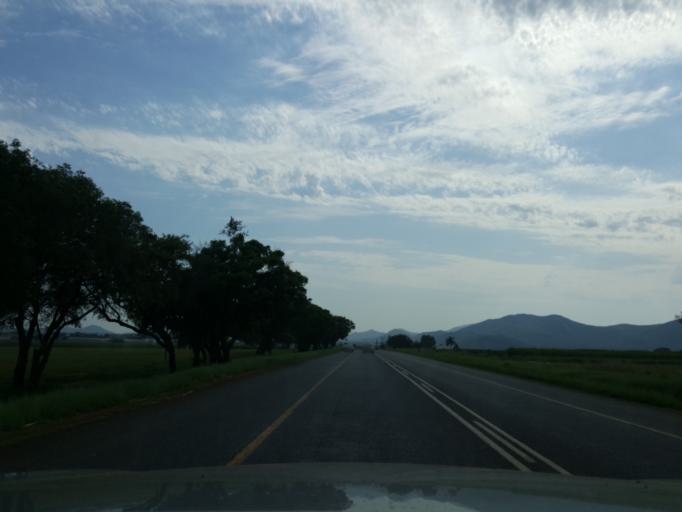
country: SZ
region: Hhohho
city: Ntfonjeni
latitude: -25.5054
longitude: 31.4940
